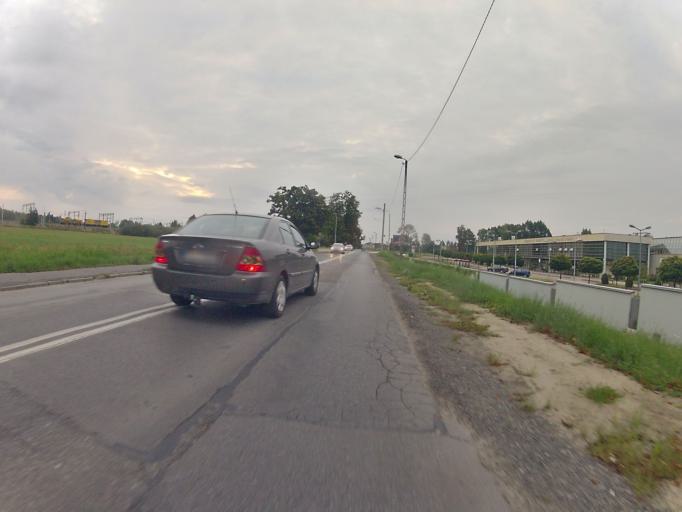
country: PL
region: Lesser Poland Voivodeship
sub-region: Powiat krakowski
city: Rzaska
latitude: 50.0809
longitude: 19.8638
